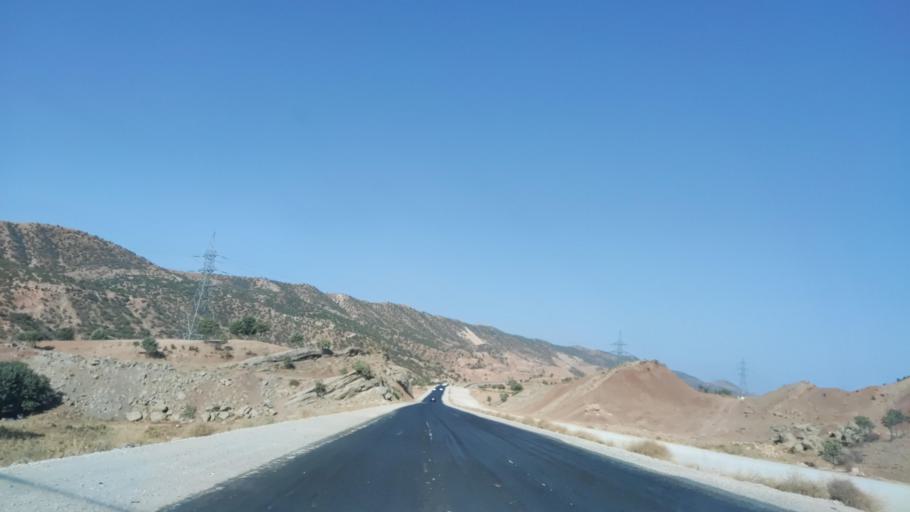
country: IQ
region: Arbil
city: Shaqlawah
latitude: 36.4298
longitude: 44.3323
